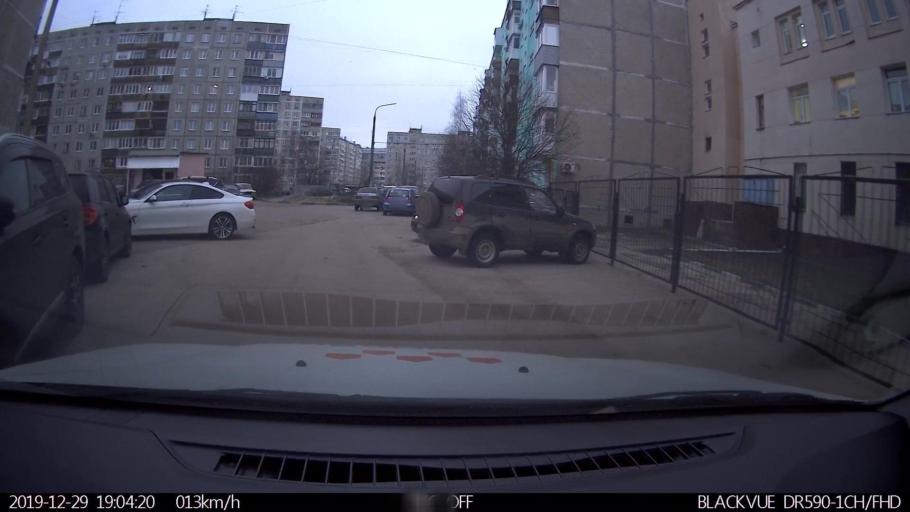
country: RU
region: Nizjnij Novgorod
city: Neklyudovo
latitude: 56.3574
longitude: 43.8574
